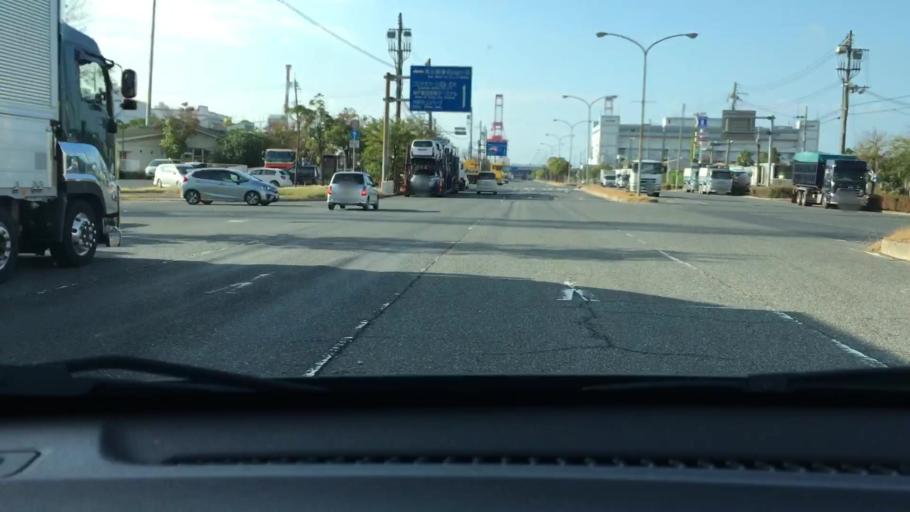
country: JP
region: Hyogo
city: Ashiya
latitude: 34.6899
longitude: 135.2775
